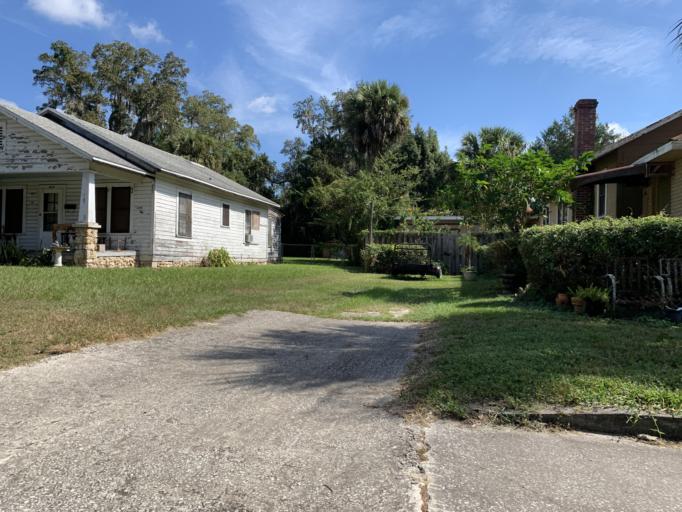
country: US
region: Florida
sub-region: Marion County
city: Ocala
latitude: 29.1781
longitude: -82.1342
